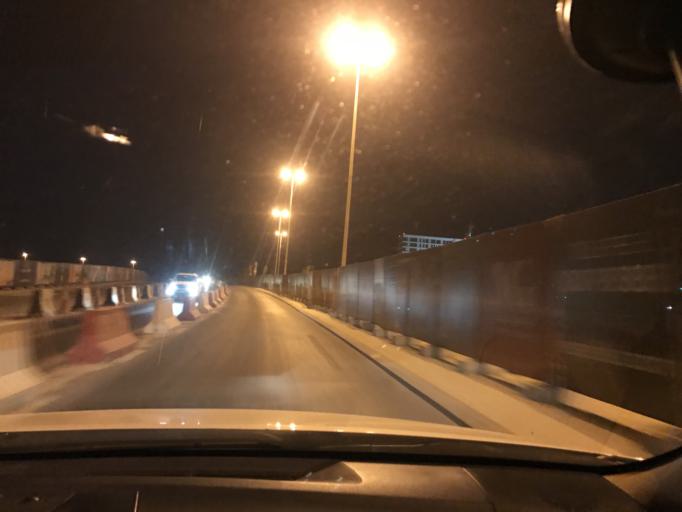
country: BH
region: Muharraq
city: Al Muharraq
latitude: 26.3013
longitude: 50.6425
